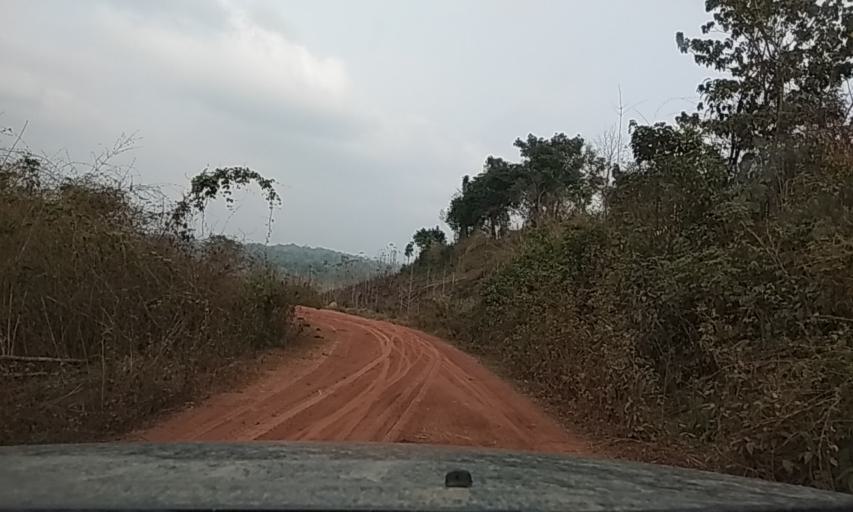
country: TH
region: Nan
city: Mae Charim
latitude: 18.4422
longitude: 101.1886
